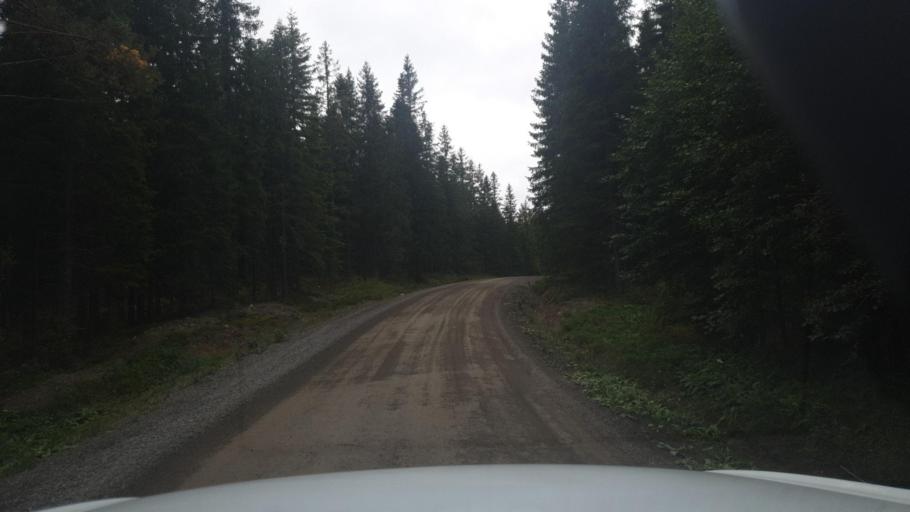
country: SE
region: Vaermland
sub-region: Sunne Kommun
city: Sunne
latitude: 59.8366
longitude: 12.9261
